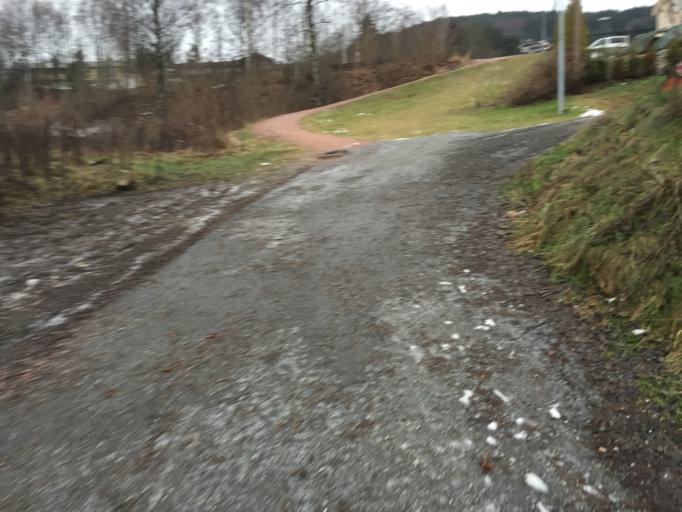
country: NO
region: Buskerud
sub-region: Drammen
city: Drammen
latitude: 59.7268
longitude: 10.2081
